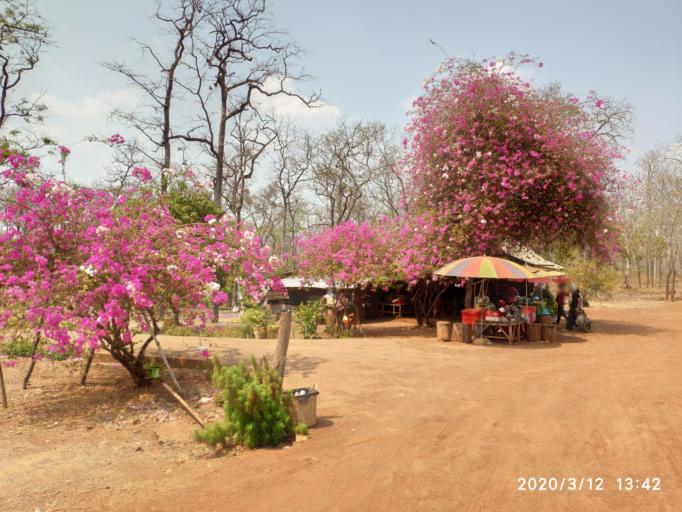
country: KH
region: Preah Vihear
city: Tbeng Meanchey
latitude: 13.7856
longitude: 104.5418
